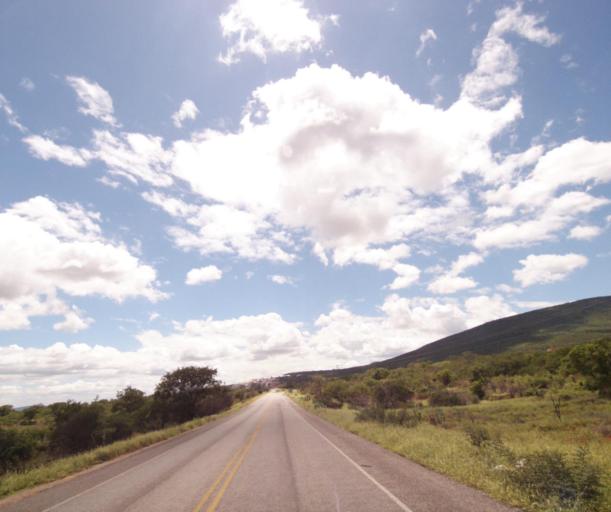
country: BR
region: Bahia
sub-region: Brumado
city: Brumado
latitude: -14.2372
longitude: -41.7113
